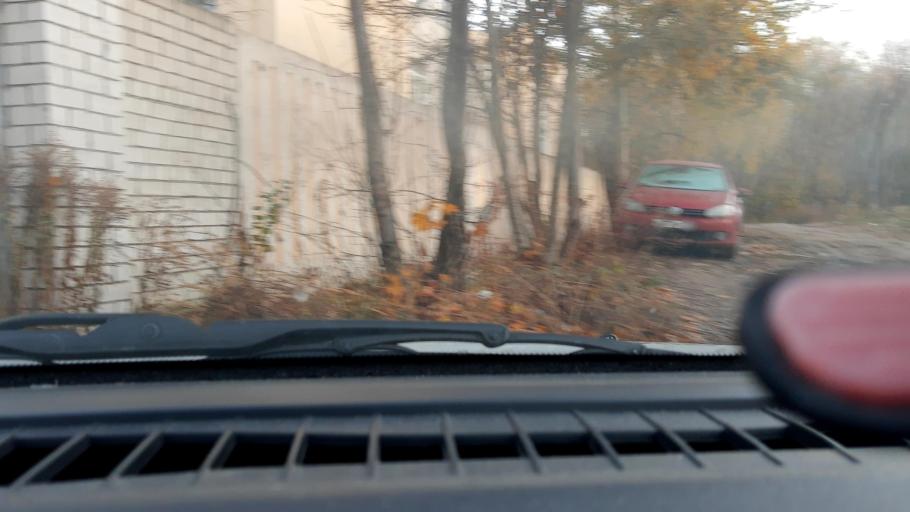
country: RU
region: Nizjnij Novgorod
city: Nizhniy Novgorod
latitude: 56.2627
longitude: 44.0034
